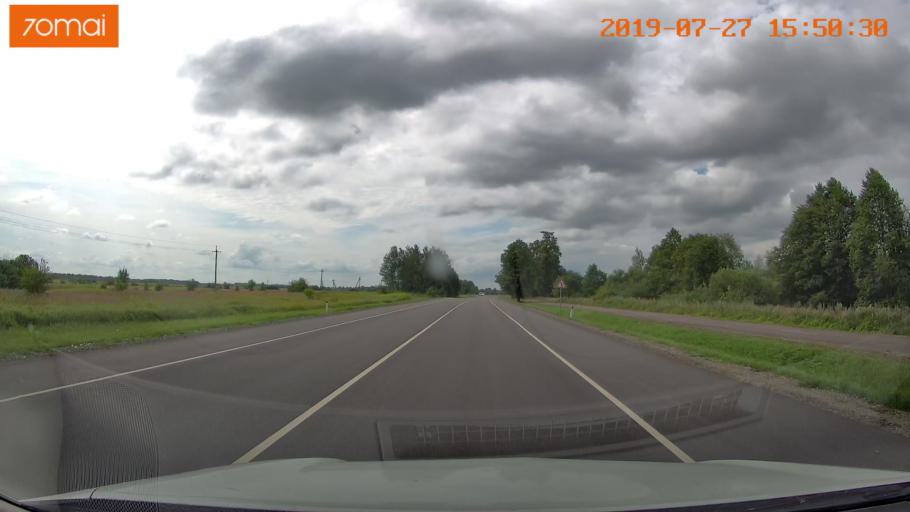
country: RU
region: Kaliningrad
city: Ozersk
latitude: 54.6009
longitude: 22.0053
